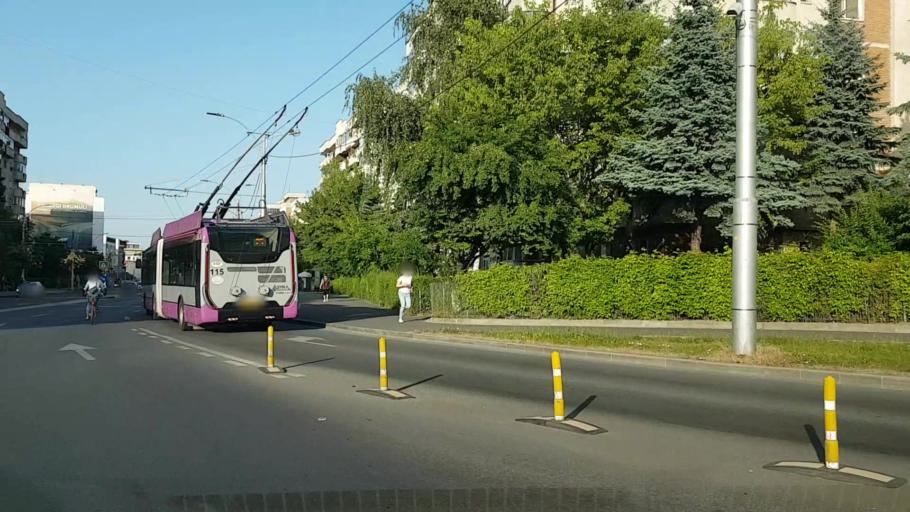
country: RO
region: Cluj
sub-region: Municipiul Cluj-Napoca
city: Cluj-Napoca
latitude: 46.7604
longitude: 23.5627
